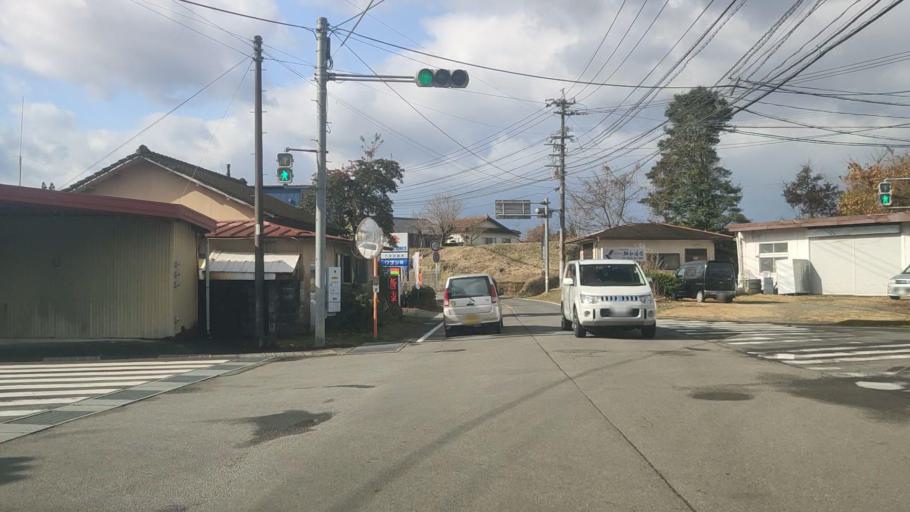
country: JP
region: Kumamoto
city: Hitoyoshi
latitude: 32.2355
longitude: 130.7904
